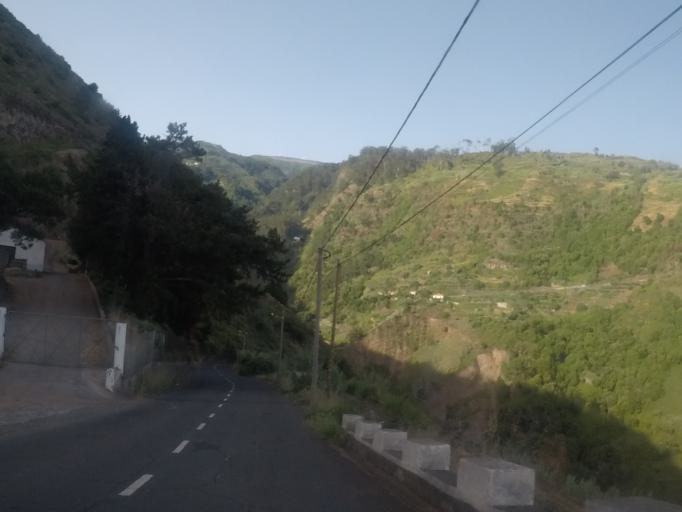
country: PT
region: Madeira
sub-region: Calheta
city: Arco da Calheta
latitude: 32.7088
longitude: -17.1363
